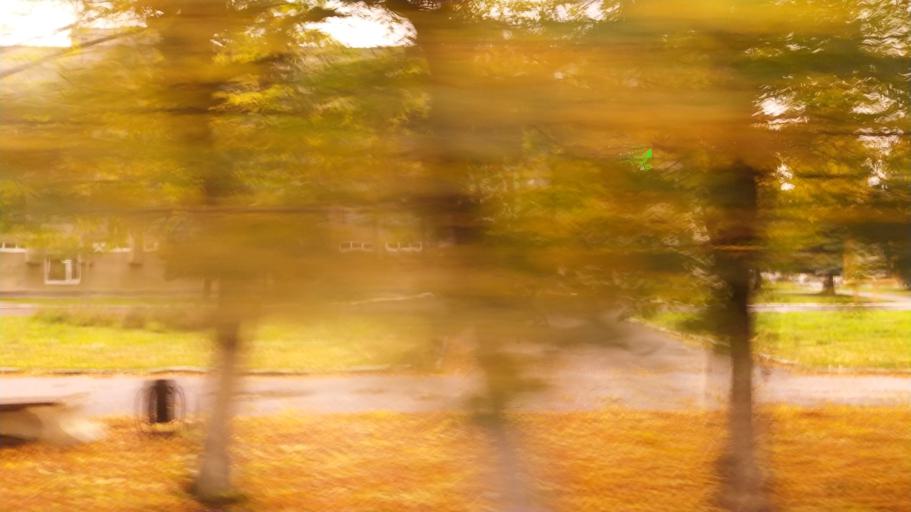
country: RU
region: Tverskaya
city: Tver
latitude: 56.8448
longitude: 35.9178
